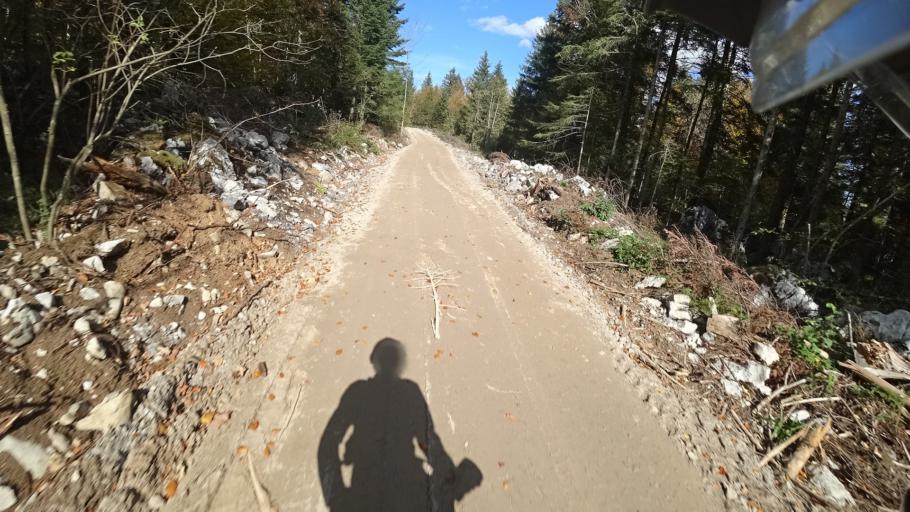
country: HR
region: Karlovacka
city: Plaski
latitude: 45.0652
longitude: 15.3436
